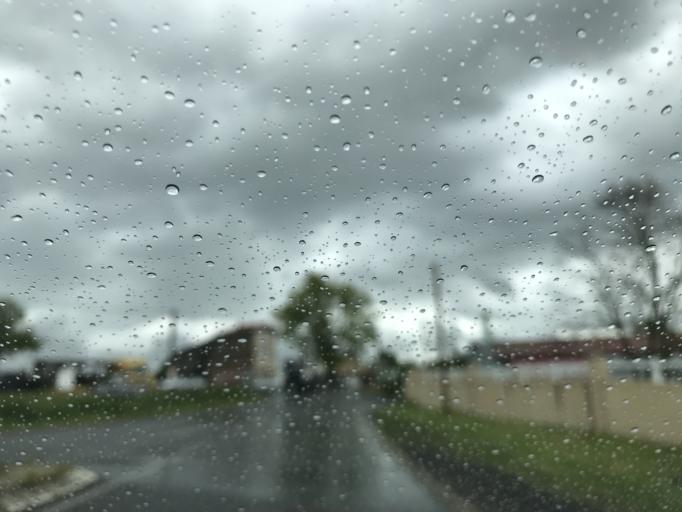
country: FR
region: Auvergne
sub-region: Departement du Puy-de-Dome
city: Montaigut
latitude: 45.6958
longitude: 3.4311
